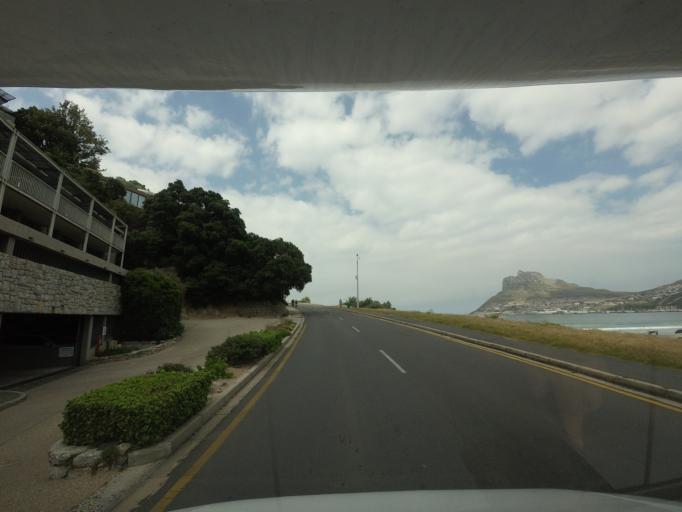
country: ZA
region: Western Cape
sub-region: City of Cape Town
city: Constantia
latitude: -34.0472
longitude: 18.3614
